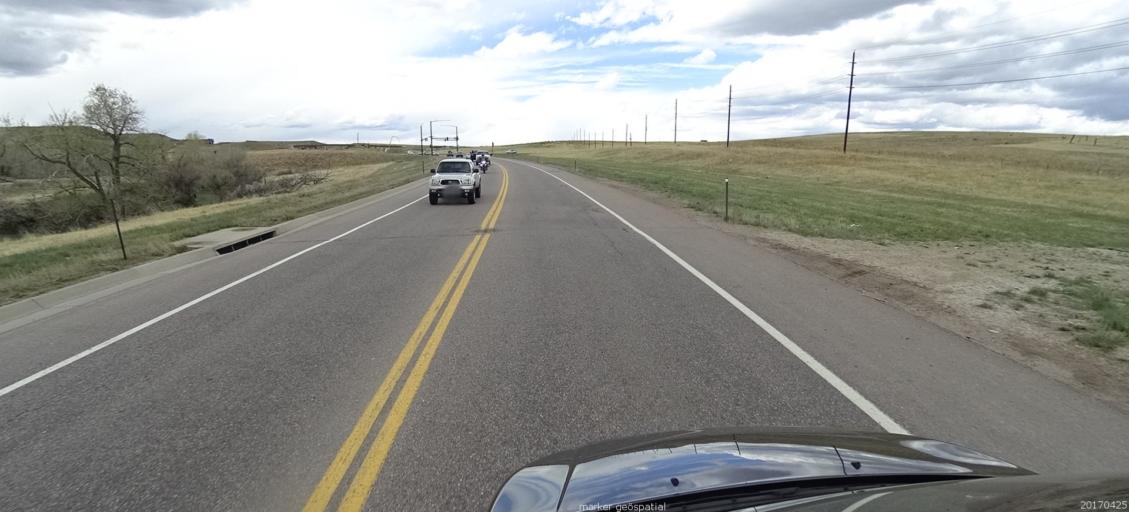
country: US
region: Colorado
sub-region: Douglas County
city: Meridian
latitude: 39.5226
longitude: -104.8543
